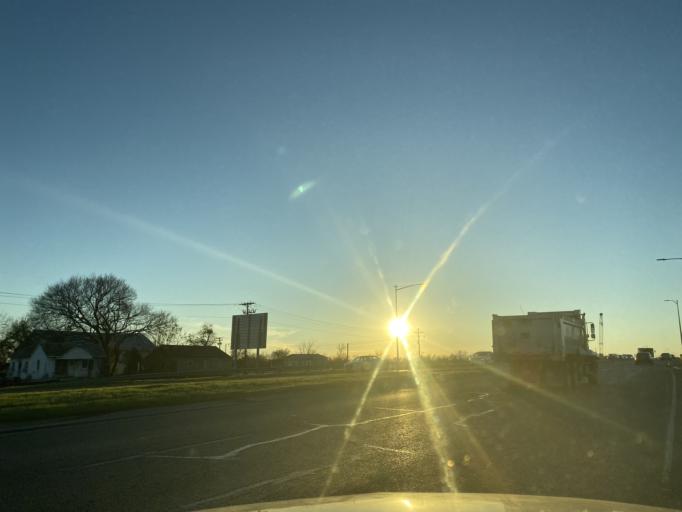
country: US
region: Texas
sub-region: Bastrop County
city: Bastrop
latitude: 30.1051
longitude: -97.3175
